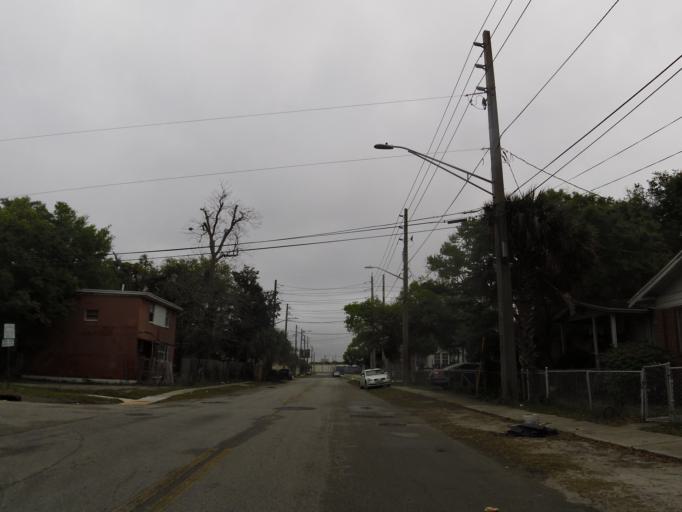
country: US
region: Florida
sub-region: Duval County
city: Jacksonville
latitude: 30.3365
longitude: -81.6405
